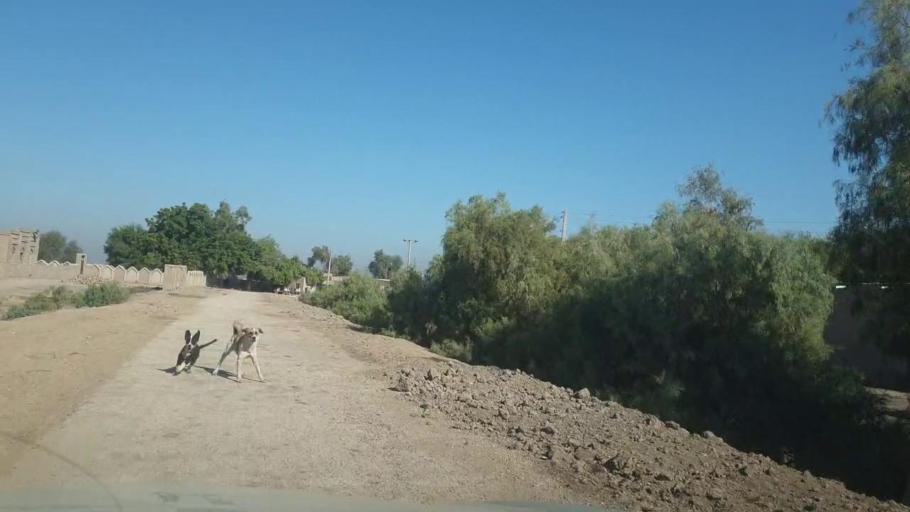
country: PK
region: Sindh
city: Bhan
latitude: 26.5504
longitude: 67.6537
